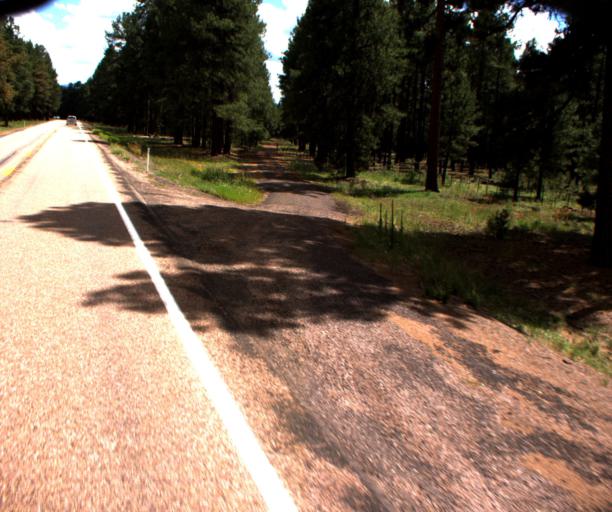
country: US
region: Arizona
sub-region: Navajo County
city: Pinetop-Lakeside
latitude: 34.0681
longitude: -109.7793
